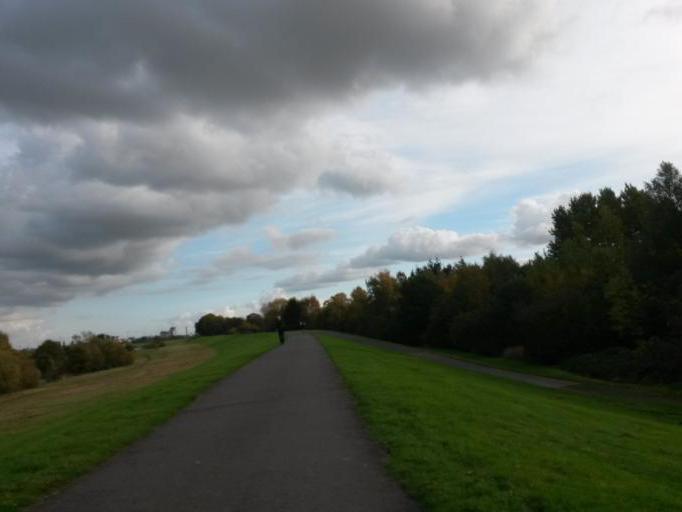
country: DE
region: Bremen
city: Bremen
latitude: 53.0546
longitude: 8.8528
